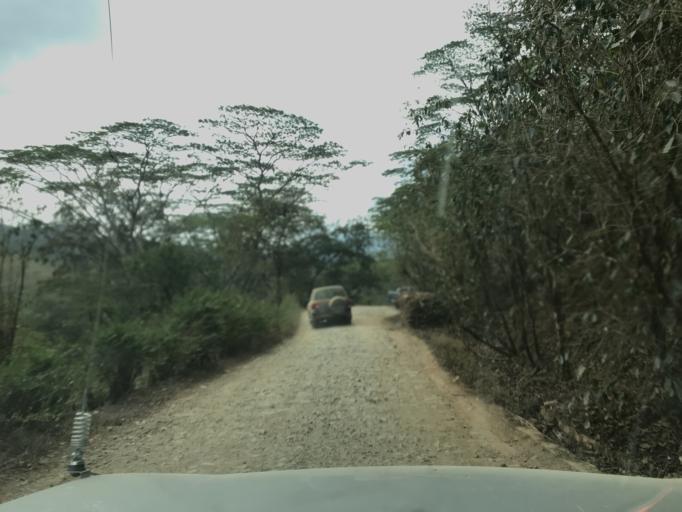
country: TL
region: Ermera
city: Gleno
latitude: -8.8250
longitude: 125.4347
